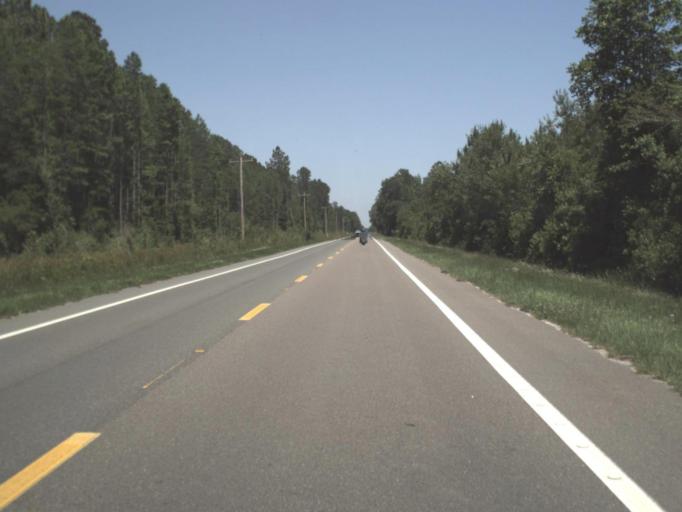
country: US
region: Florida
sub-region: Baker County
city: Macclenny
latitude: 30.2637
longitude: -82.2292
